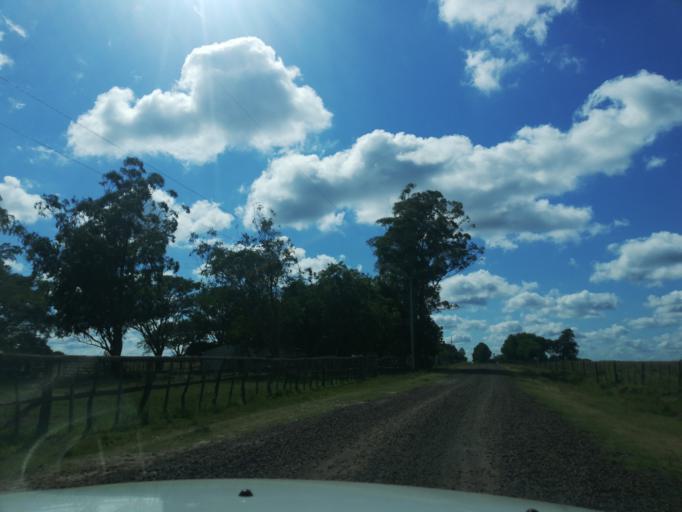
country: AR
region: Corrientes
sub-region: Departamento de San Miguel
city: San Miguel
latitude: -27.9815
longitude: -57.5800
